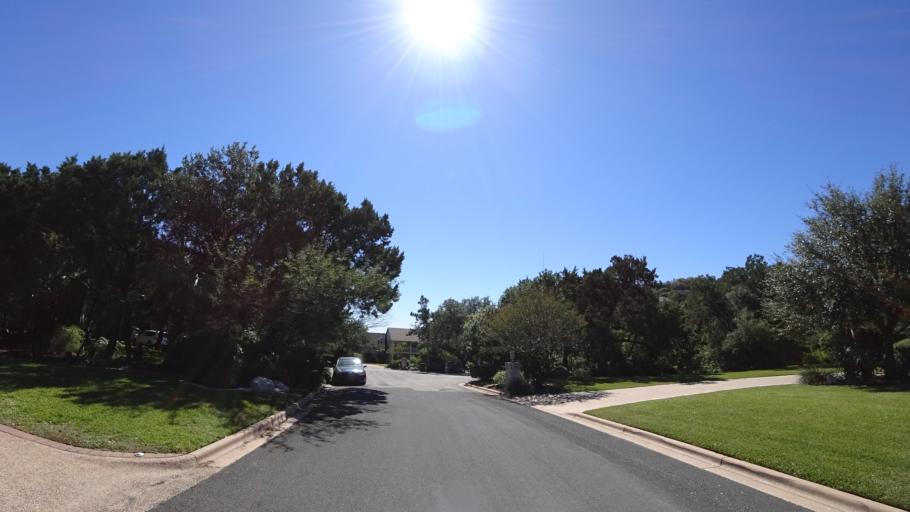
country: US
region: Texas
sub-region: Travis County
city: West Lake Hills
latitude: 30.3243
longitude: -97.7881
